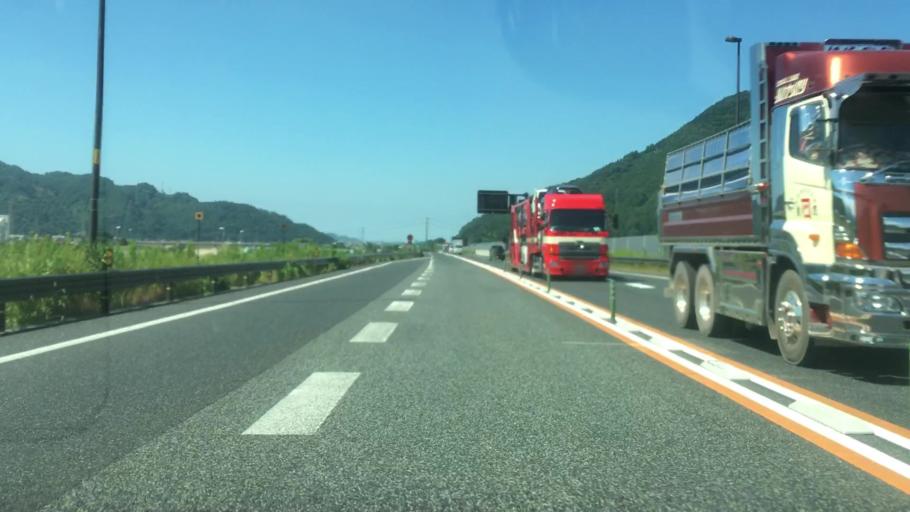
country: JP
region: Tottori
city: Tottori
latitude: 35.3983
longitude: 134.2049
